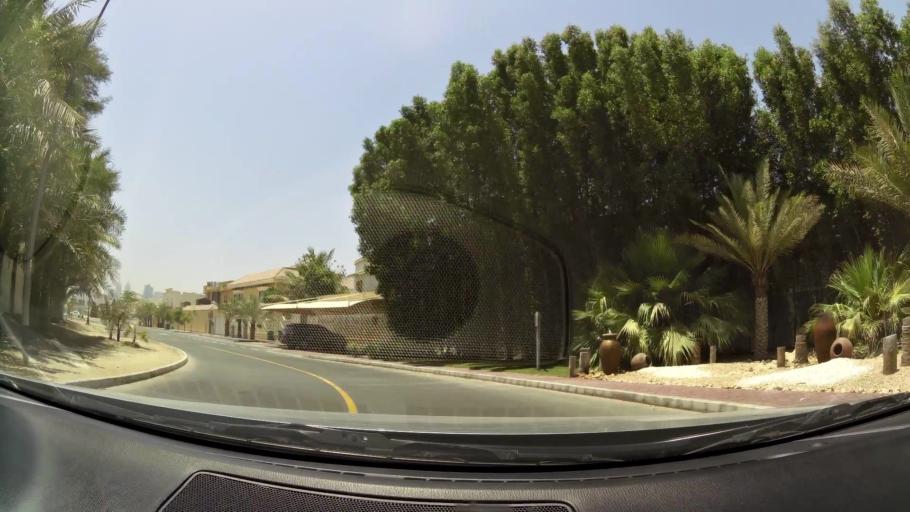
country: AE
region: Dubai
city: Dubai
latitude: 25.0991
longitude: 55.1989
